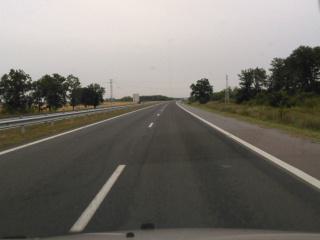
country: BG
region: Stara Zagora
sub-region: Obshtina Stara Zagora
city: Stara Zagora
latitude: 42.3423
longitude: 25.6775
